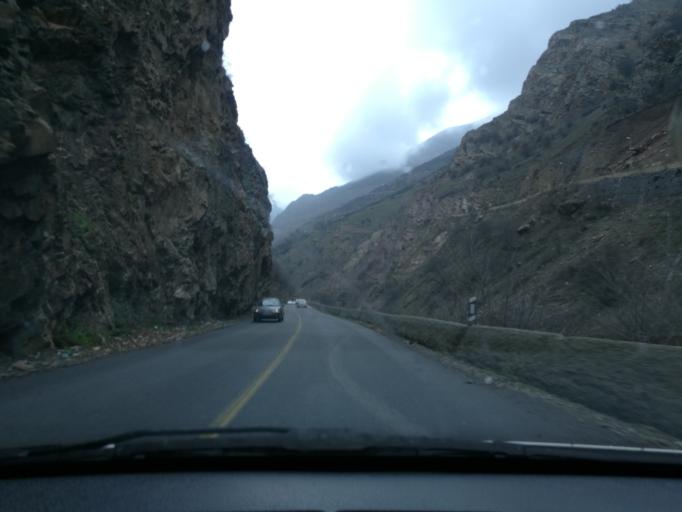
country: IR
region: Mazandaran
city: Chalus
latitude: 36.2618
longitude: 51.2654
